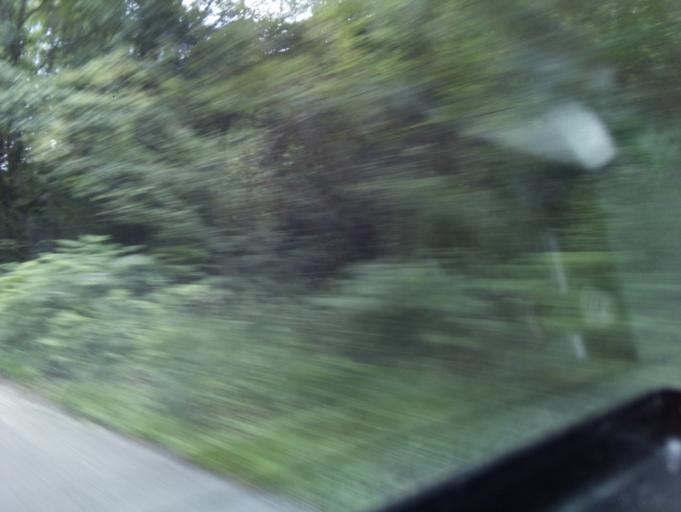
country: GB
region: England
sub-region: Gloucestershire
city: Cinderford
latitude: 51.8061
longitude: -2.4904
